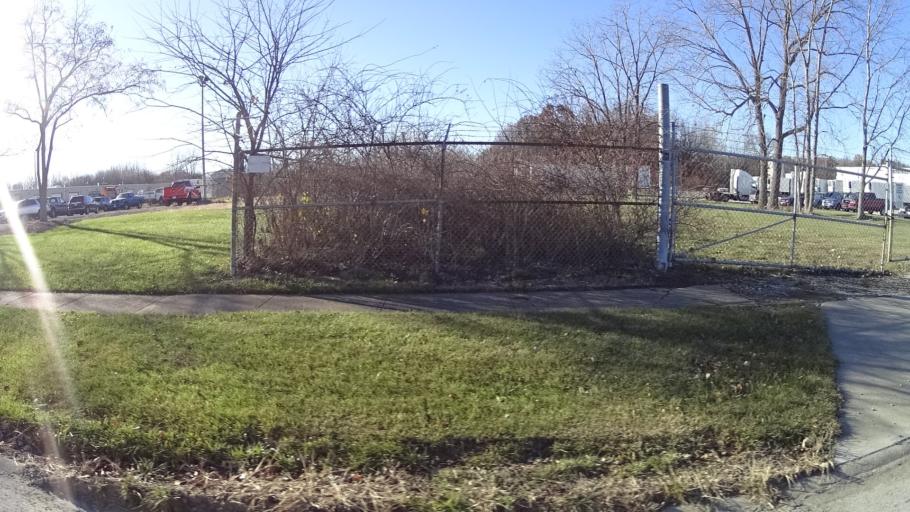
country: US
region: Ohio
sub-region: Lorain County
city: Elyria
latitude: 41.3609
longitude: -82.1237
